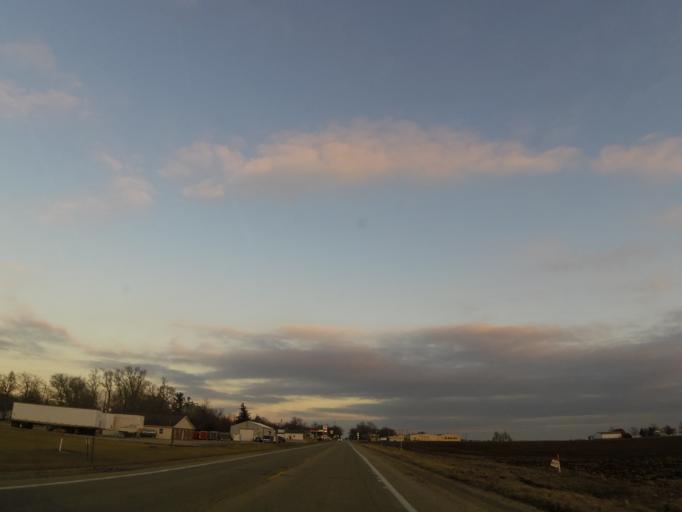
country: US
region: Illinois
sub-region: McLean County
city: Gridley
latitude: 40.7396
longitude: -88.8878
